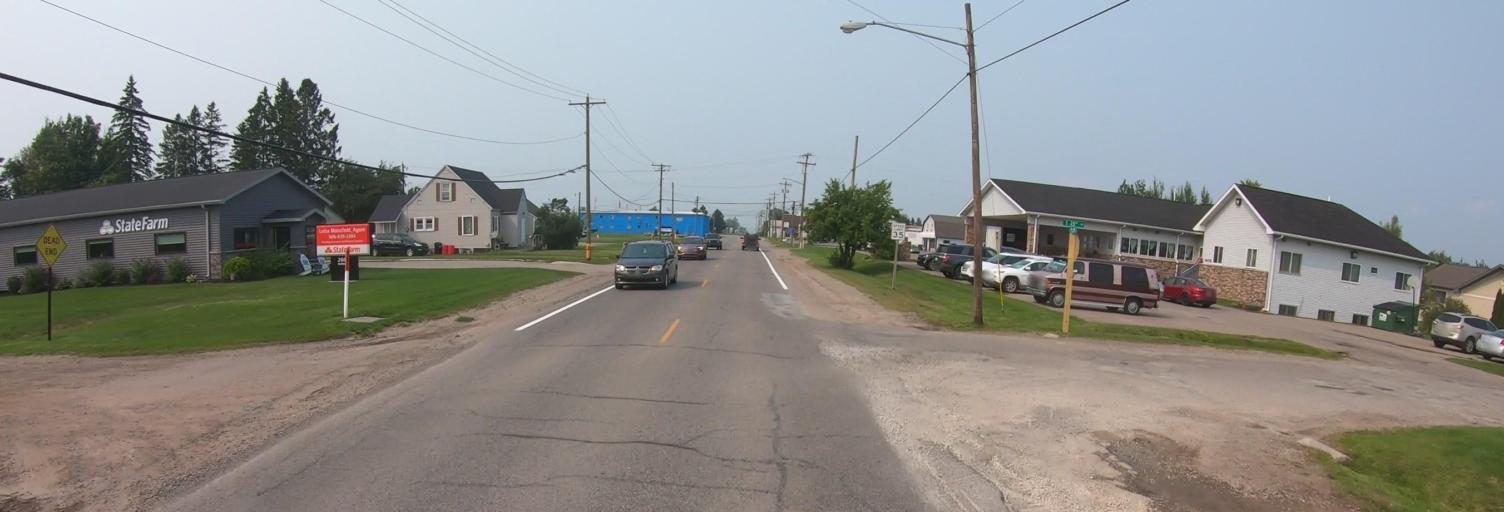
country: US
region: Michigan
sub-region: Chippewa County
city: Sault Ste. Marie
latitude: 46.4737
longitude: -84.3539
